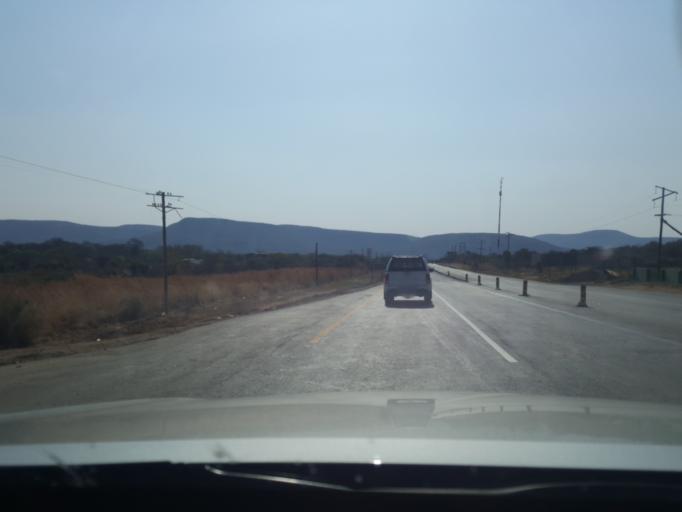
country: ZA
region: North-West
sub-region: Ngaka Modiri Molema District Municipality
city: Zeerust
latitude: -25.5958
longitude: 26.4243
